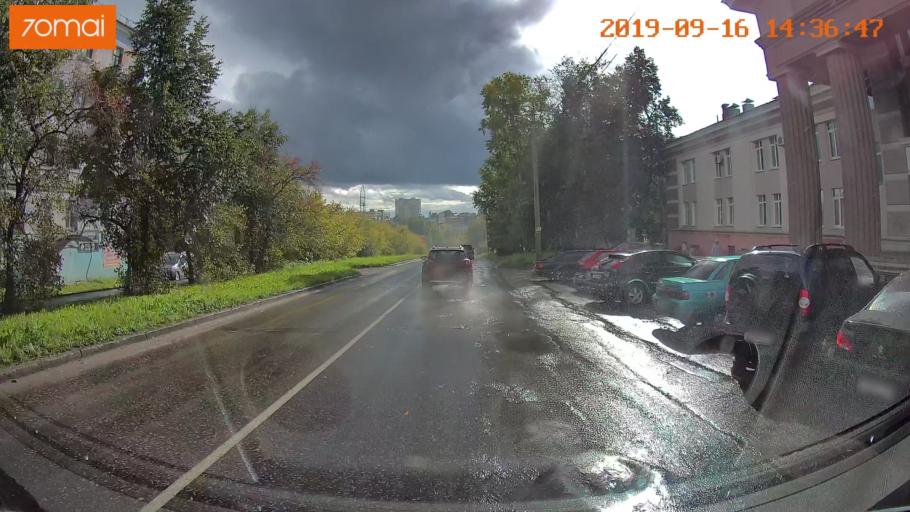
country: RU
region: Ivanovo
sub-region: Gorod Ivanovo
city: Ivanovo
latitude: 57.0168
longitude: 40.9570
